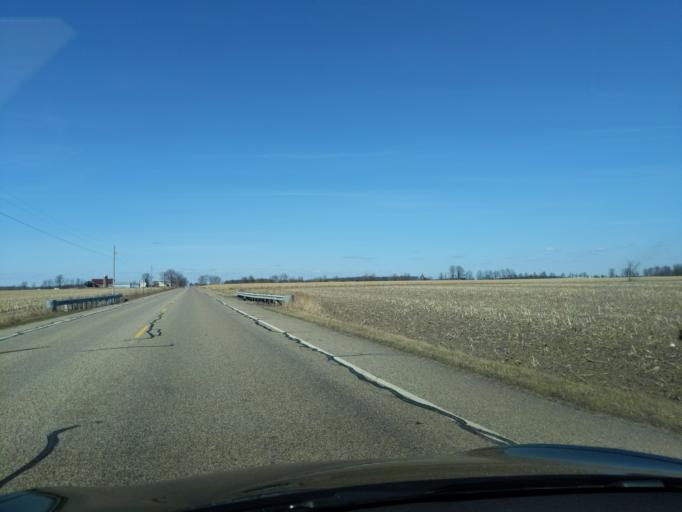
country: US
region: Michigan
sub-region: Ionia County
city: Lake Odessa
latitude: 42.8588
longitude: -85.1342
